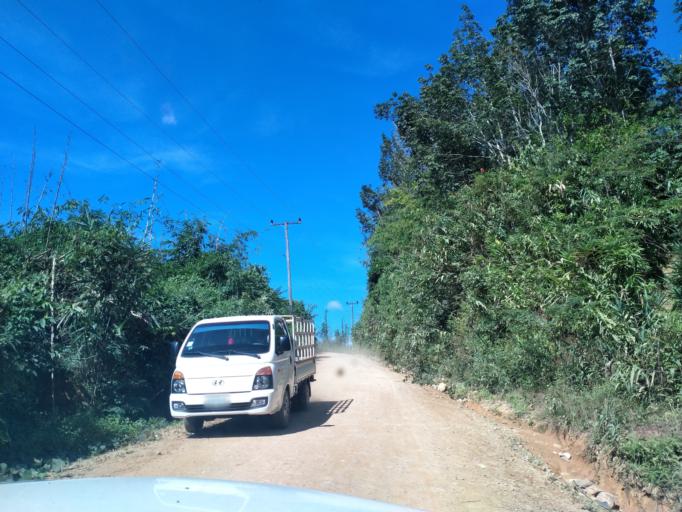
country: TH
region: Changwat Bueng Kan
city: Pak Khat
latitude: 18.6294
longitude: 103.0721
